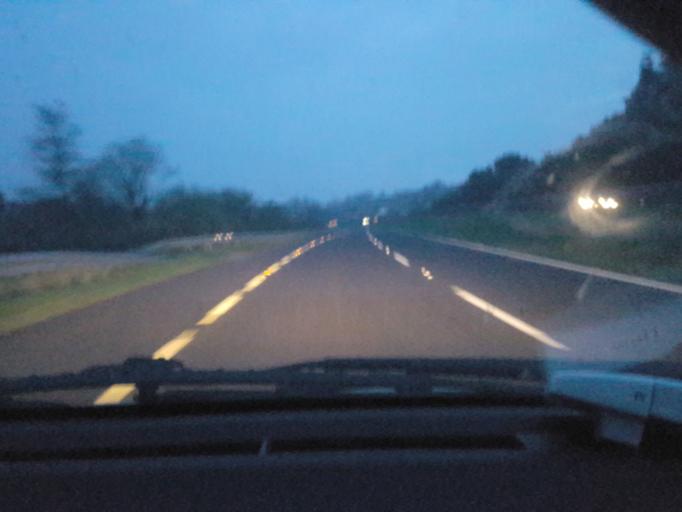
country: IE
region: Munster
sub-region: County Cork
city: Cork
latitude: 51.8463
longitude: -8.5284
